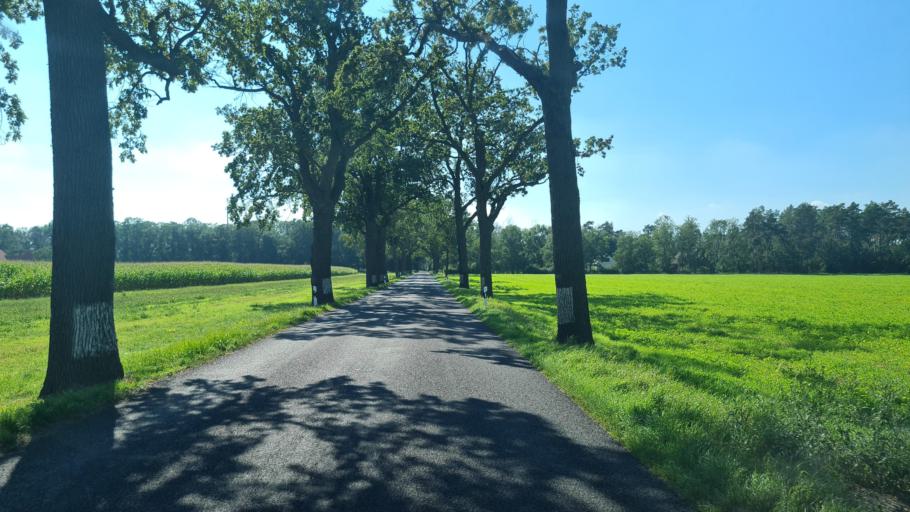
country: DE
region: Brandenburg
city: Retzow
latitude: 52.6476
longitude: 12.6922
